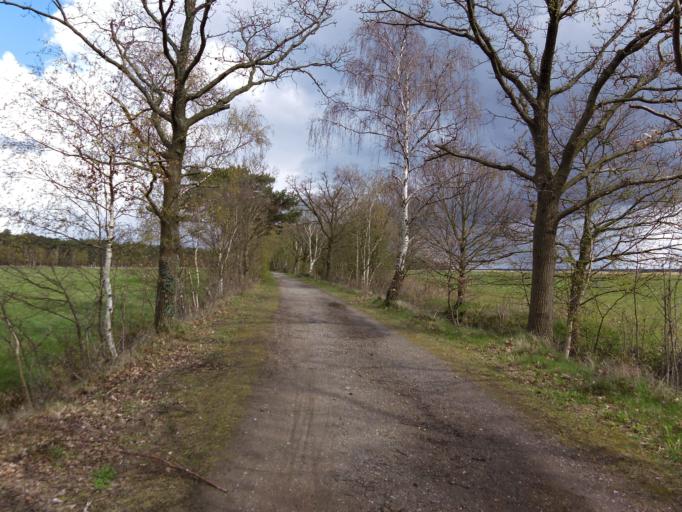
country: DE
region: Mecklenburg-Vorpommern
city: Born
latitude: 54.3916
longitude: 12.5587
